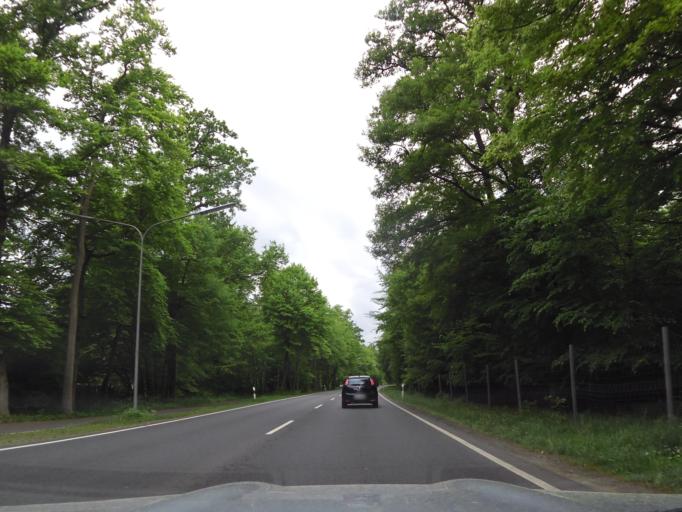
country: DE
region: Hesse
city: Morfelden-Walldorf
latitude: 49.9732
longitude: 8.5444
